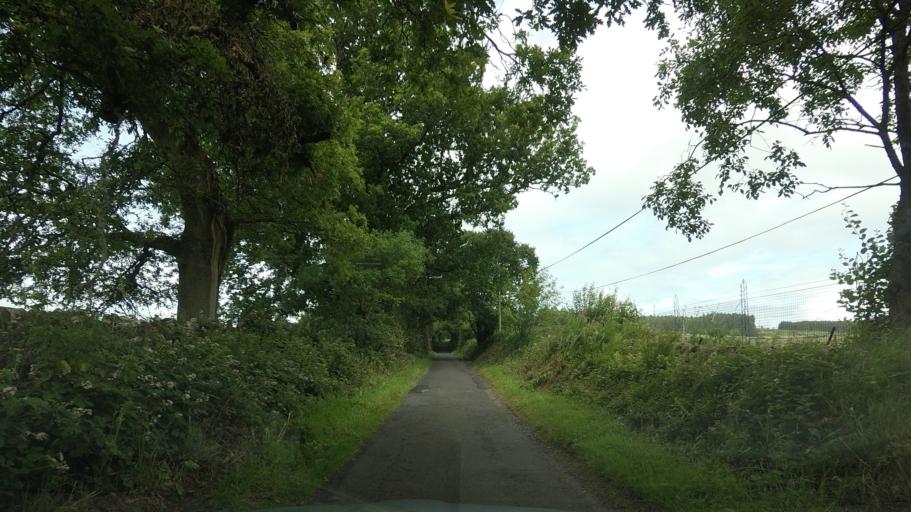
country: GB
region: Scotland
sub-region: Stirling
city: Killearn
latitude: 56.0773
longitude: -4.4500
